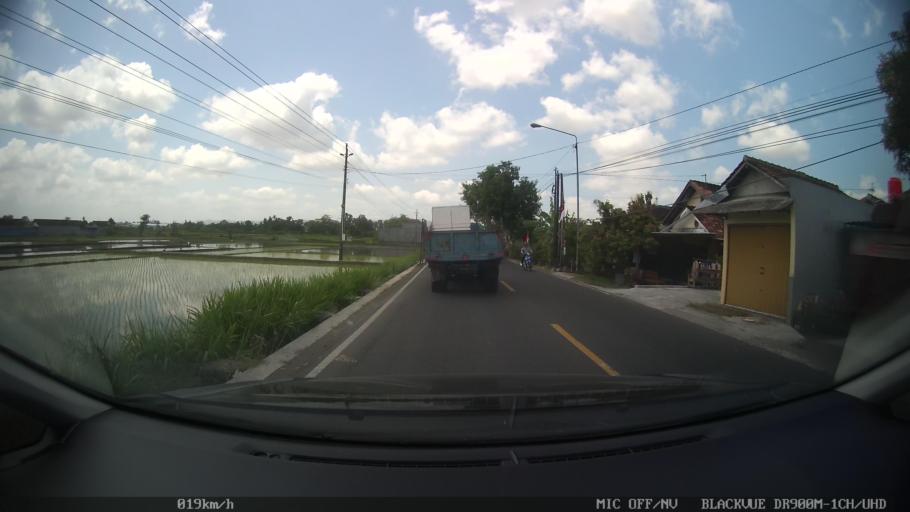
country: ID
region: Daerah Istimewa Yogyakarta
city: Bantul
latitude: -7.9066
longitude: 110.3397
